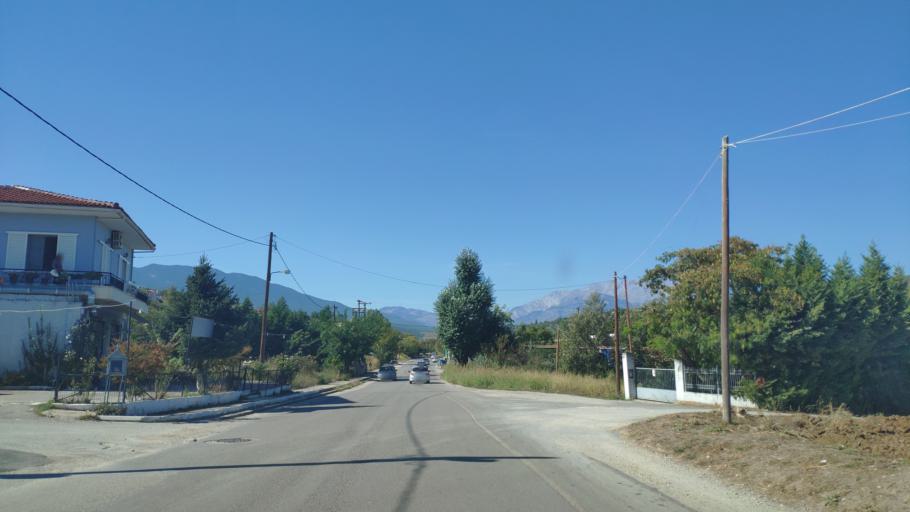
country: GR
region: Central Greece
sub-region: Nomos Voiotias
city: Livadeia
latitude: 38.4435
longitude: 22.8618
